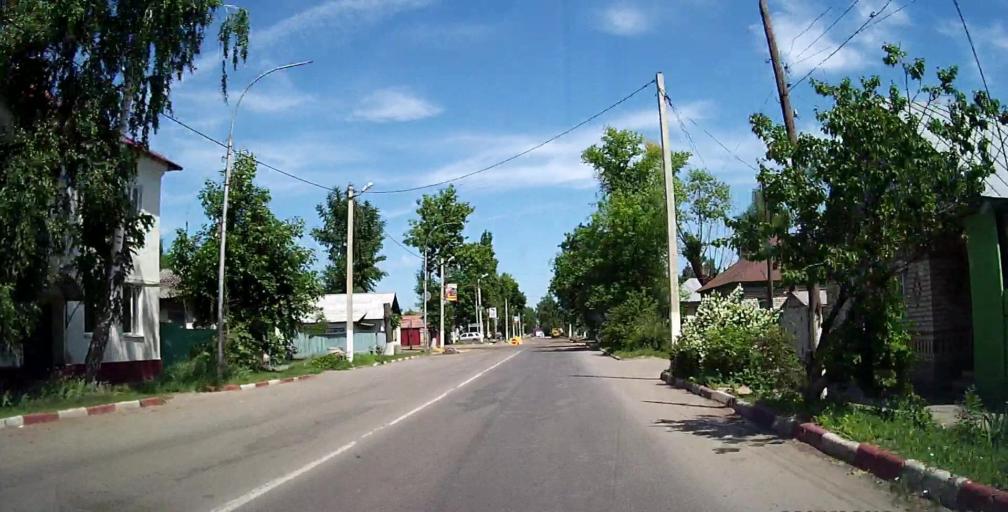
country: RU
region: Lipetsk
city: Chaplygin
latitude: 53.2422
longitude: 39.9718
